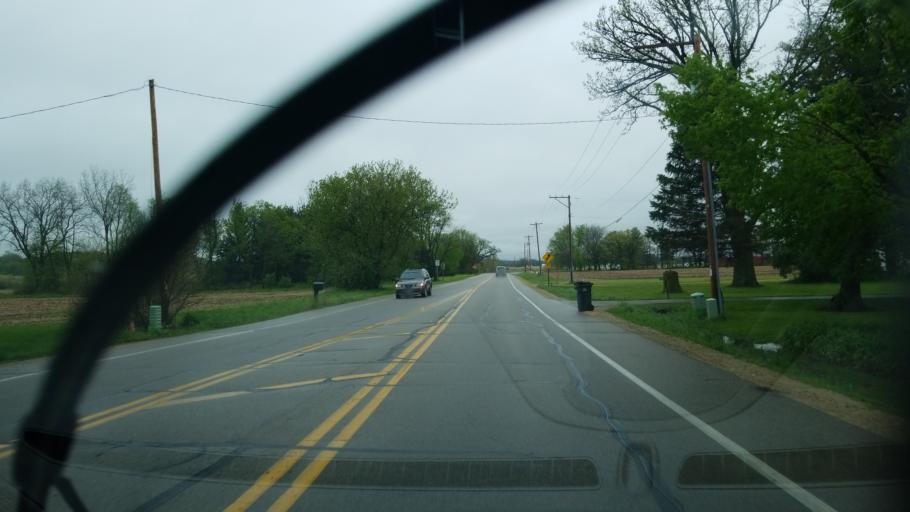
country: US
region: Wisconsin
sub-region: Dane County
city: Fitchburg
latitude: 42.9497
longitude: -89.4373
